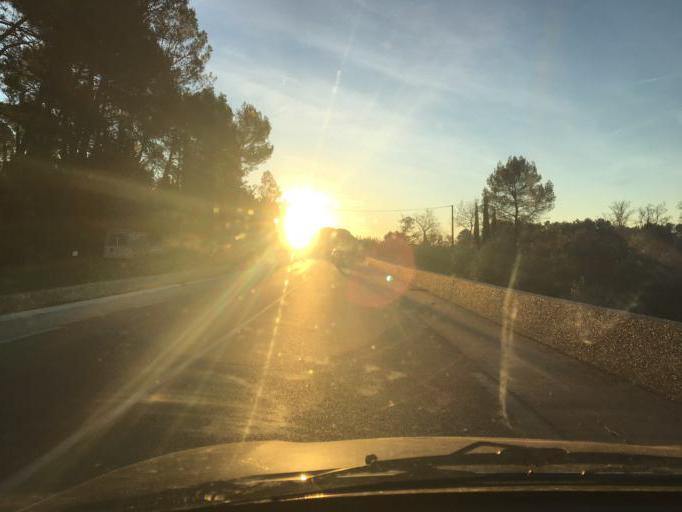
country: FR
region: Provence-Alpes-Cote d'Azur
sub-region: Departement du Var
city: Taradeau
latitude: 43.4632
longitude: 6.4009
